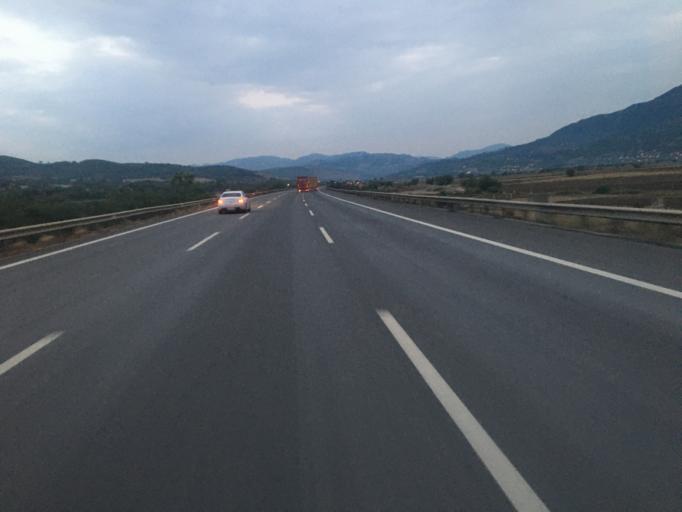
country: TR
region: Osmaniye
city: Osmaniye
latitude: 37.1405
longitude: 36.3200
